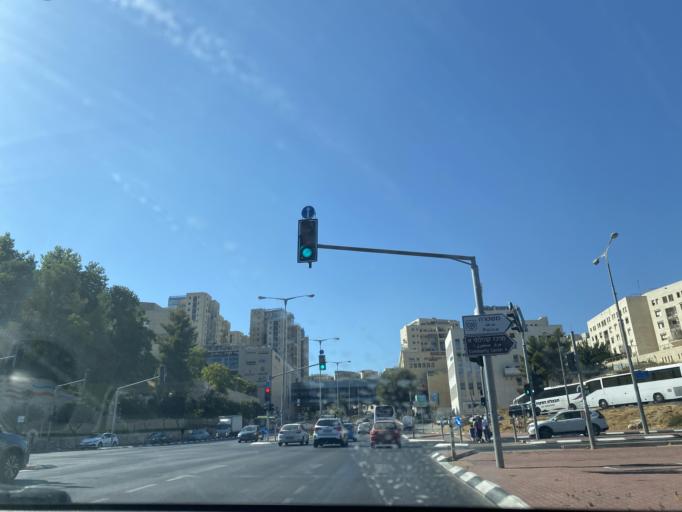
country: PS
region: West Bank
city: Bayt Iksa
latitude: 31.8152
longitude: 35.1962
